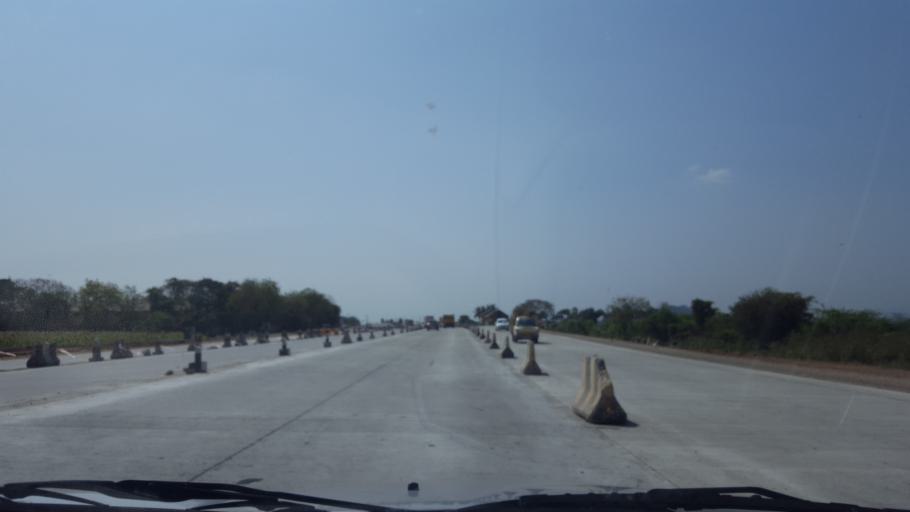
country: IN
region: Andhra Pradesh
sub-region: Prakasam
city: Addanki
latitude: 15.7623
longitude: 80.0323
